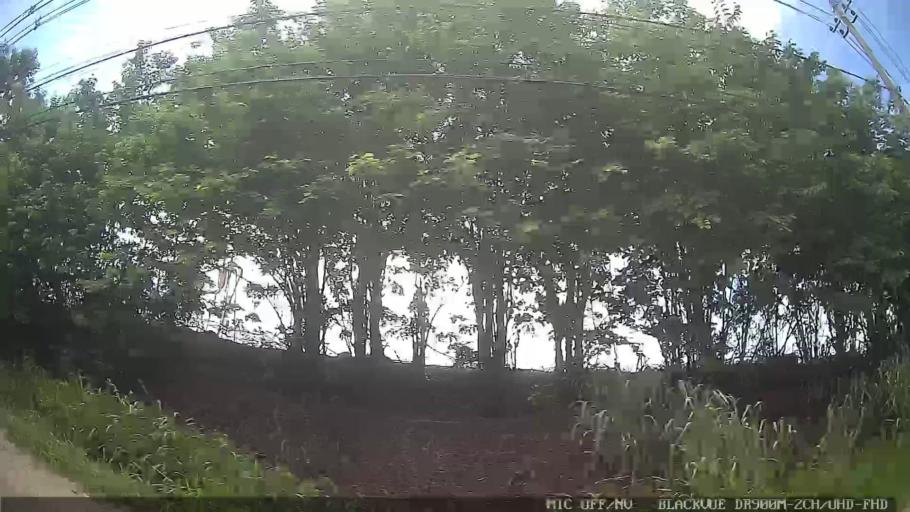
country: BR
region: Sao Paulo
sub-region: Santa Isabel
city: Santa Isabel
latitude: -23.4173
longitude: -46.2145
